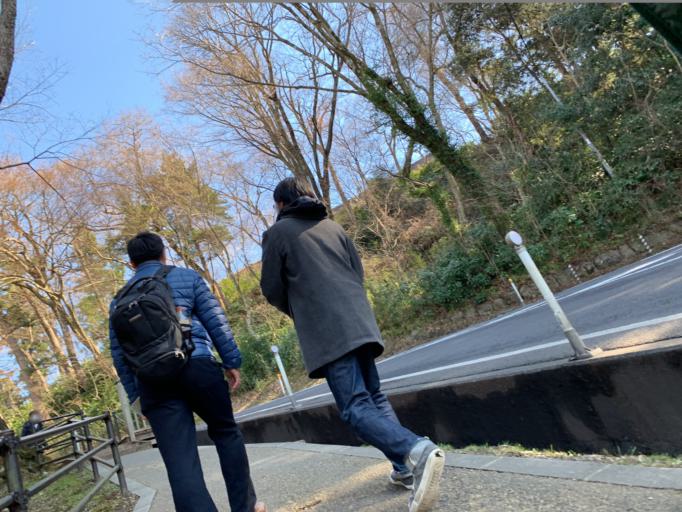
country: JP
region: Miyagi
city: Sendai
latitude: 38.2544
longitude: 140.8557
